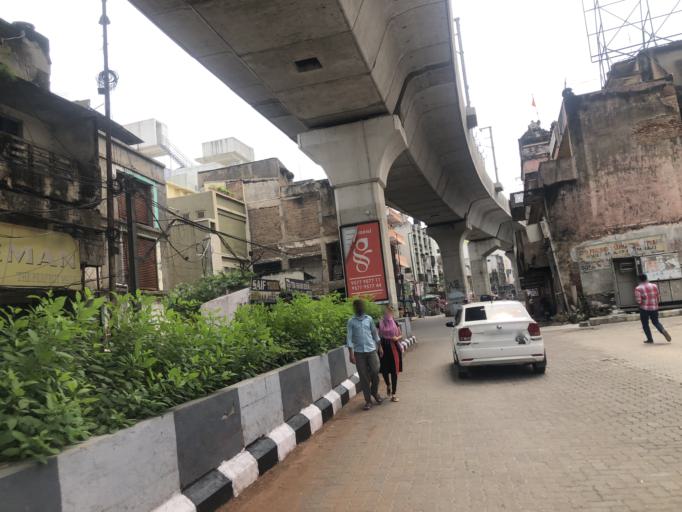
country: IN
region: Telangana
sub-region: Hyderabad
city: Hyderabad
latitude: 17.3904
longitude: 78.4889
